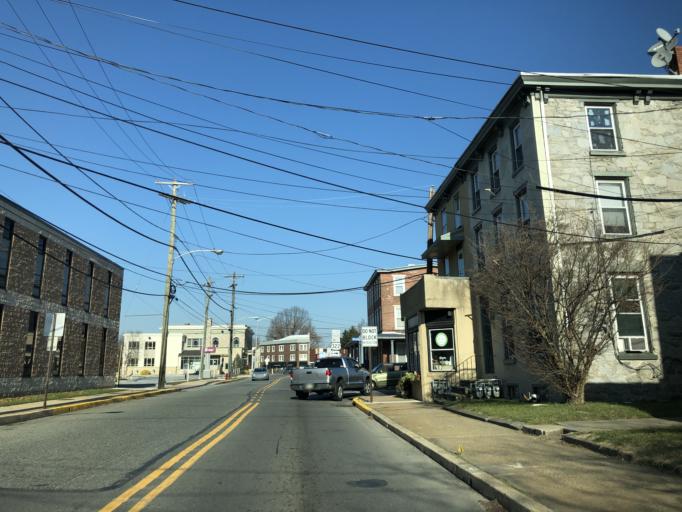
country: US
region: Pennsylvania
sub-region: Chester County
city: Downingtown
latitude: 40.0053
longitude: -75.7029
